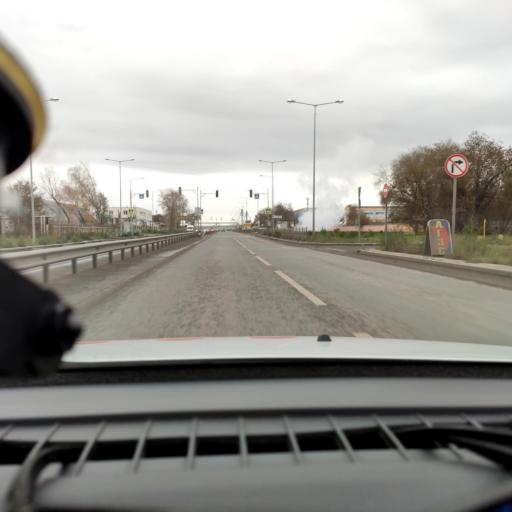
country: RU
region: Samara
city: Smyshlyayevka
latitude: 53.1913
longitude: 50.2955
